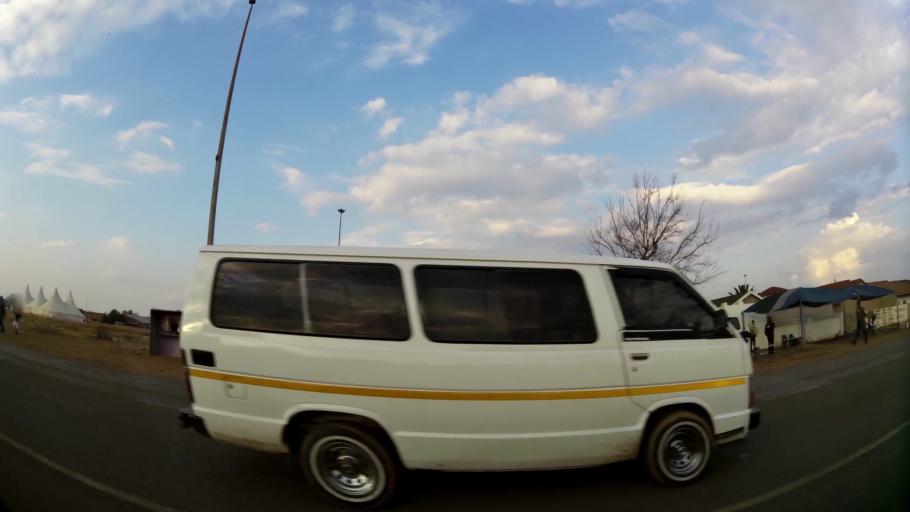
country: ZA
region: Gauteng
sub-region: City of Johannesburg Metropolitan Municipality
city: Orange Farm
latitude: -26.5913
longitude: 27.8471
